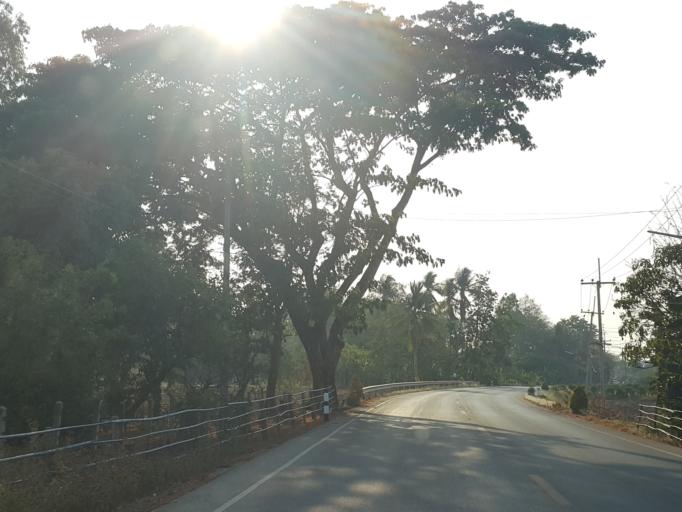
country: TH
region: Uttaradit
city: Phichai
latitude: 17.1686
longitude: 100.0909
